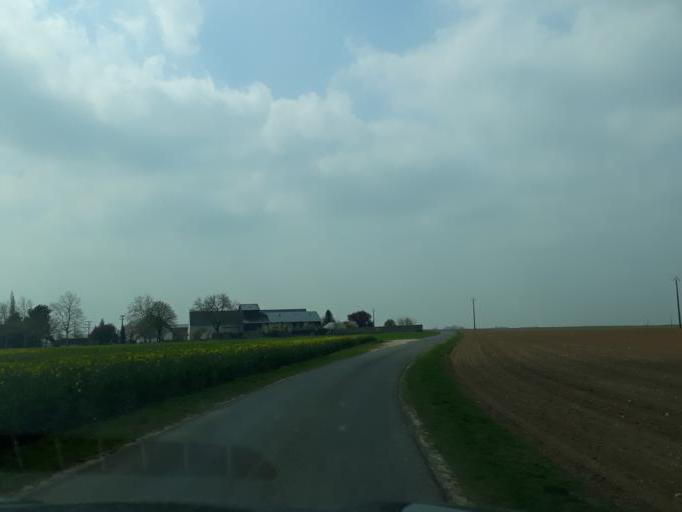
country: FR
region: Centre
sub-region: Departement d'Eure-et-Loir
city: Baigneaux
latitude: 48.0803
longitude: 1.8101
